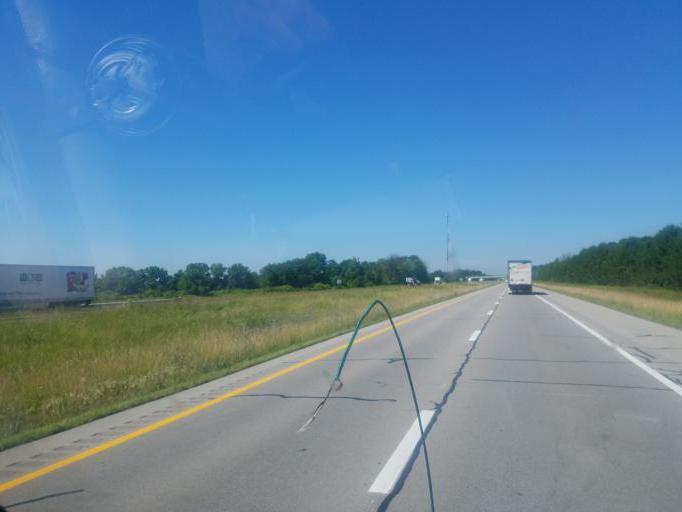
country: US
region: Ohio
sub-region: Clinton County
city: Wilmington
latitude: 39.5047
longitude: -83.8872
